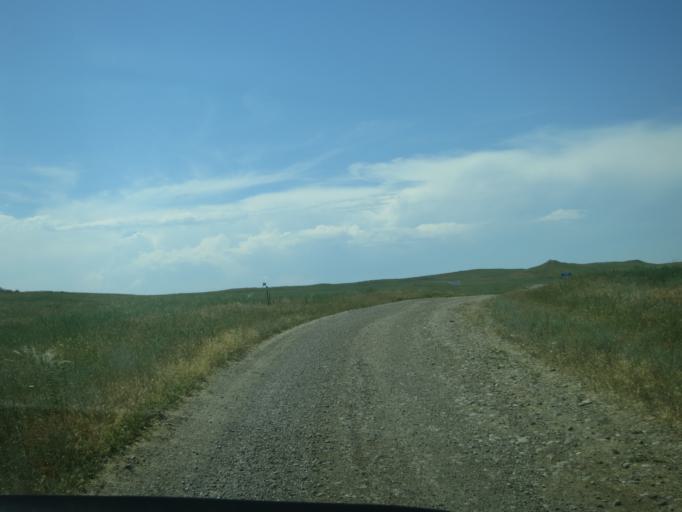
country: AZ
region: Agstafa
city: Saloglu
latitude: 41.4692
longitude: 45.3199
